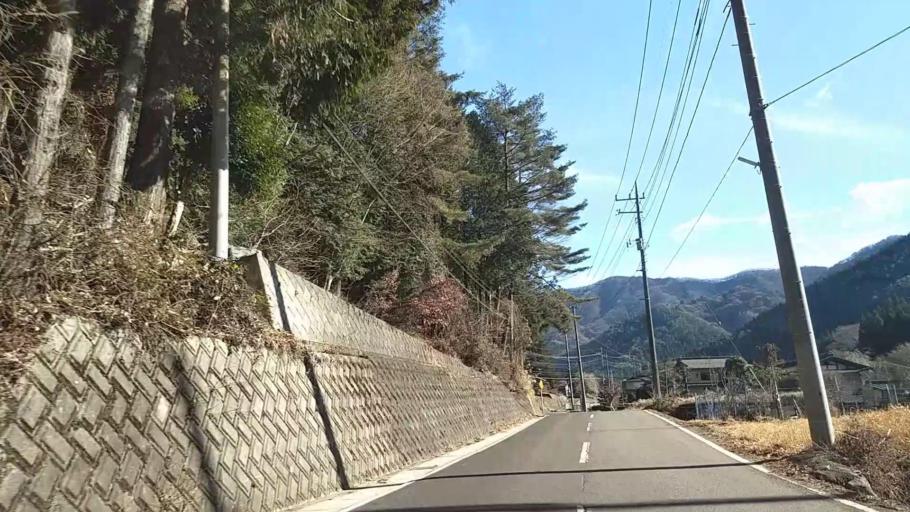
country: JP
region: Yamanashi
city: Otsuki
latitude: 35.5179
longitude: 138.9372
